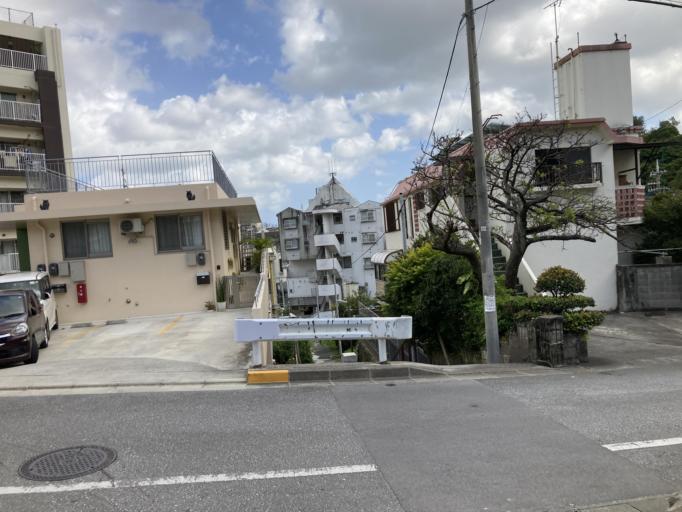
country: JP
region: Okinawa
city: Naha-shi
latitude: 26.2006
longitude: 127.6724
